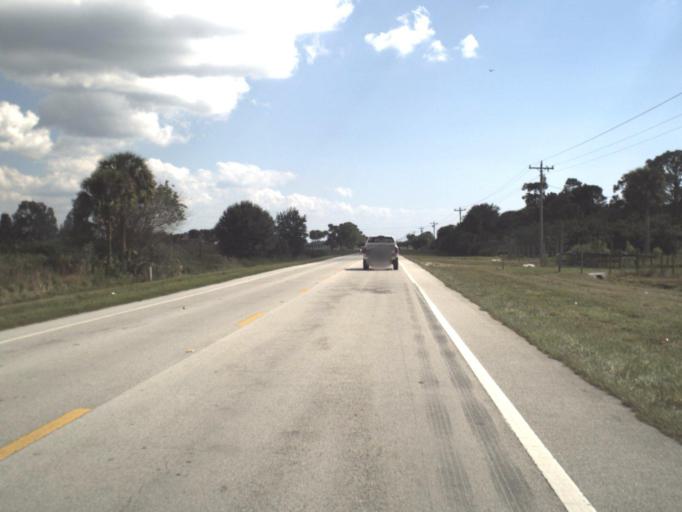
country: US
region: Florida
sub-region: Okeechobee County
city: Okeechobee
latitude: 27.2999
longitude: -80.8950
